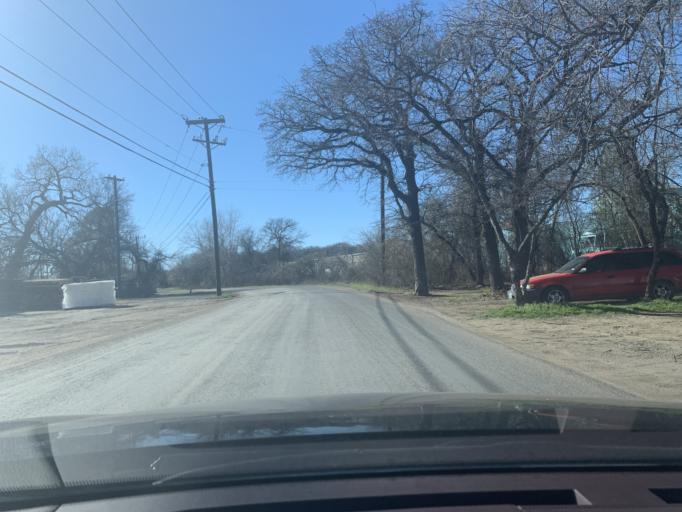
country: US
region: Texas
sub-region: Tarrant County
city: Haltom City
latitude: 32.7766
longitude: -97.2762
